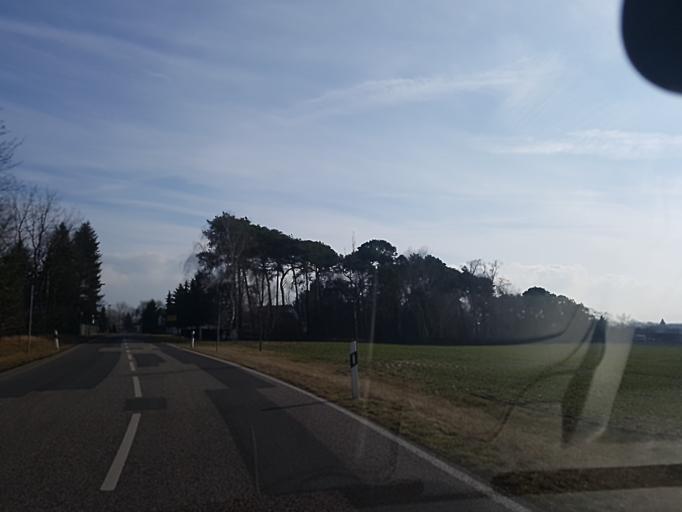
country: DE
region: Brandenburg
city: Wenzlow
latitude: 52.3046
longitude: 12.4432
